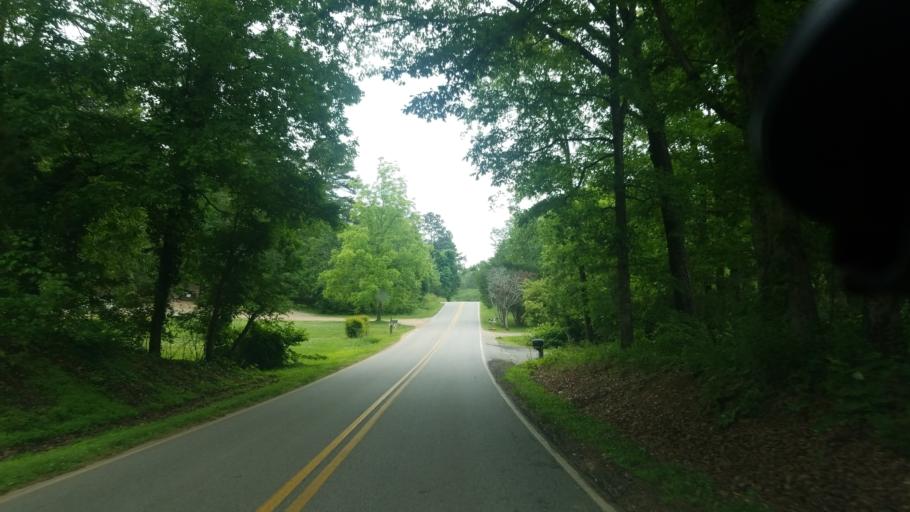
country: US
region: Georgia
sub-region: Forsyth County
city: Cumming
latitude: 34.1620
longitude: -84.1248
